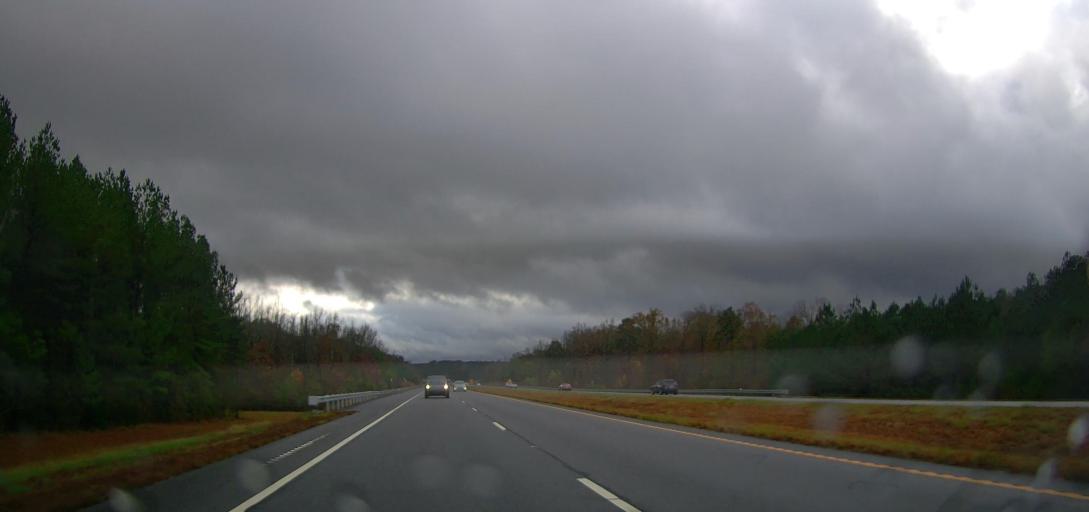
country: US
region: Georgia
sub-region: Jackson County
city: Nicholson
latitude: 34.0741
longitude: -83.4234
